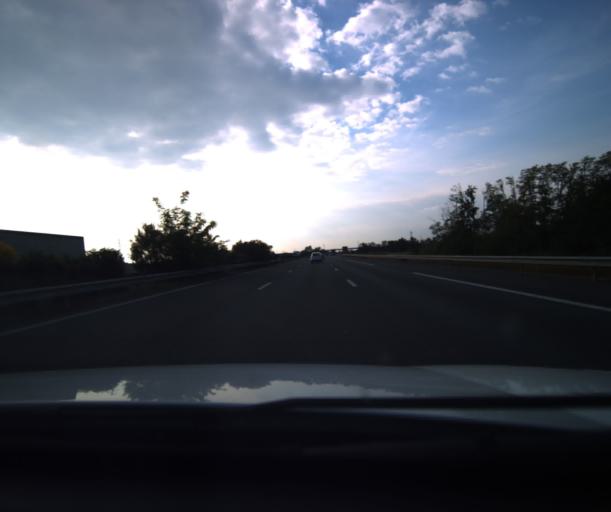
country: FR
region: Midi-Pyrenees
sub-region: Departement du Tarn-et-Garonne
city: Pompignan
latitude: 43.8411
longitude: 1.3286
